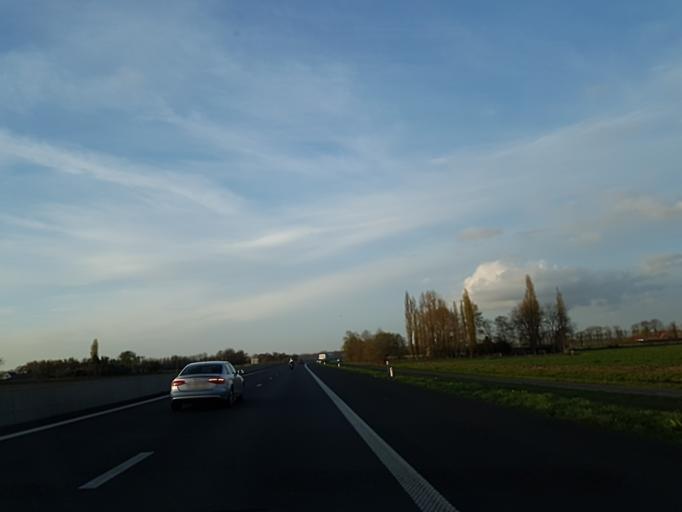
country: BE
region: Flanders
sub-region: Provincie West-Vlaanderen
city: Oostkamp
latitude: 51.1311
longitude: 3.1943
